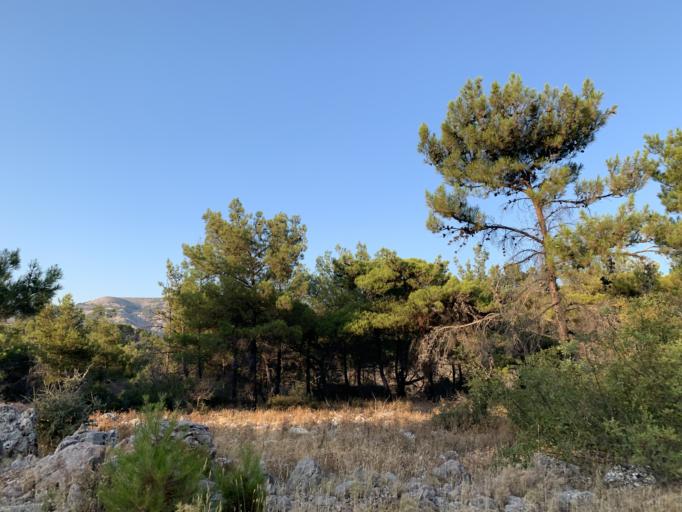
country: GR
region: North Aegean
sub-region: Chios
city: Vrontados
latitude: 38.3802
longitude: 26.0189
